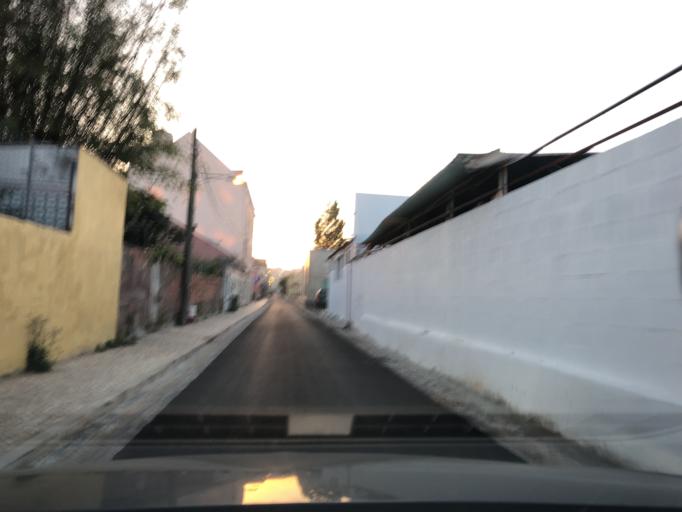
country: PT
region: Lisbon
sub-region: Oeiras
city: Alges
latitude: 38.6947
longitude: -9.2198
